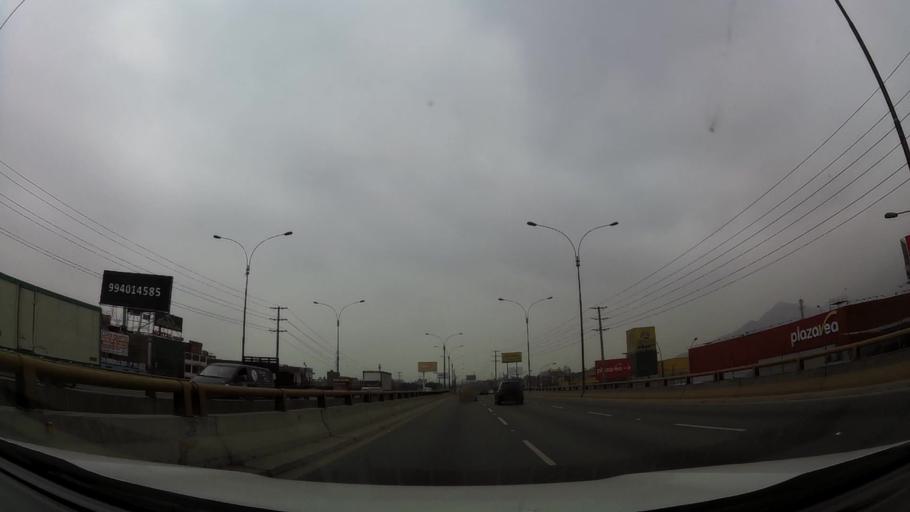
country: PE
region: Lima
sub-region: Lima
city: Independencia
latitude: -11.9899
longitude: -77.0642
